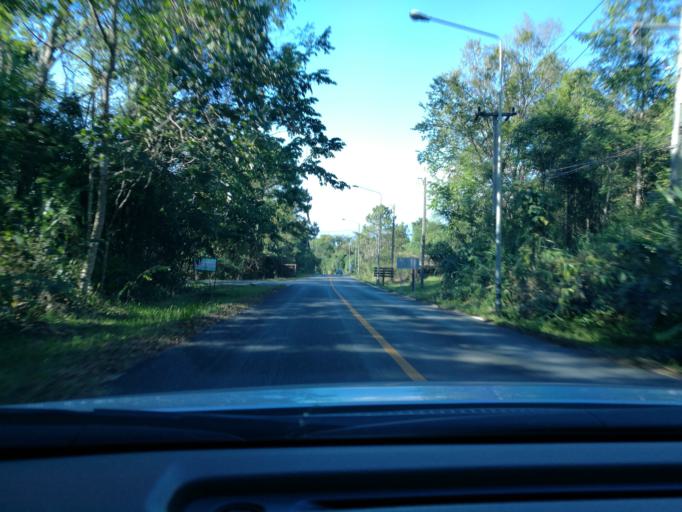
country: TH
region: Phitsanulok
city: Nakhon Thai
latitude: 16.9972
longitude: 101.0023
